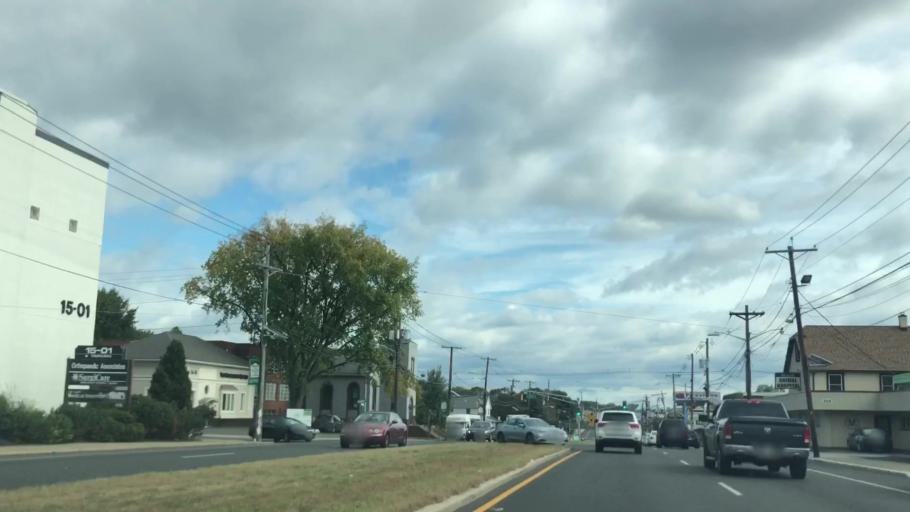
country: US
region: New Jersey
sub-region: Bergen County
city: Elmwood Park
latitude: 40.9208
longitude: -74.1187
